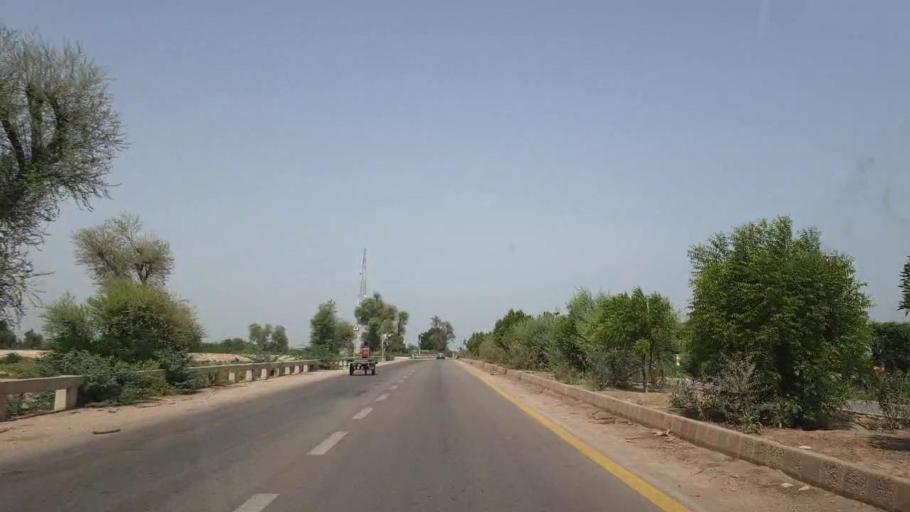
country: PK
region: Sindh
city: Sakrand
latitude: 26.1970
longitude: 68.3040
